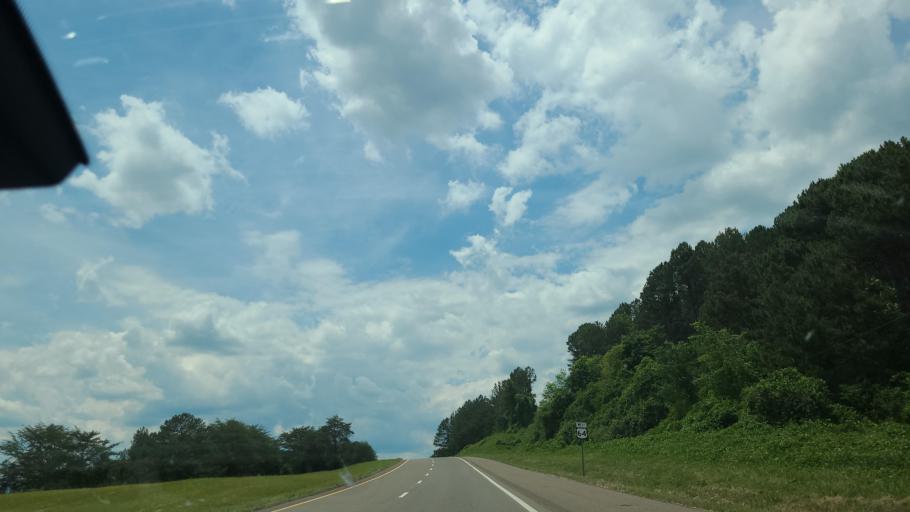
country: US
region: Georgia
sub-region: Fannin County
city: McCaysville
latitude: 35.0236
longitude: -84.3606
